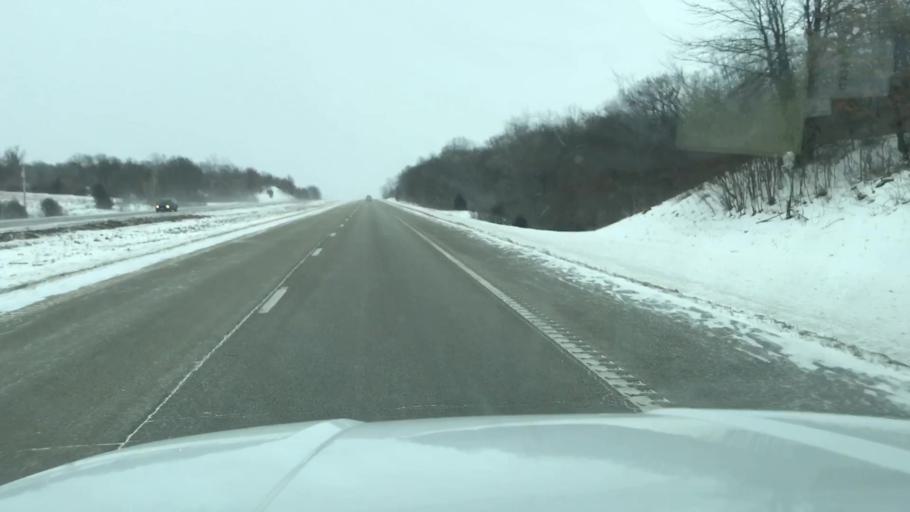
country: US
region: Missouri
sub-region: Clinton County
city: Gower
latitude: 39.7516
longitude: -94.5937
